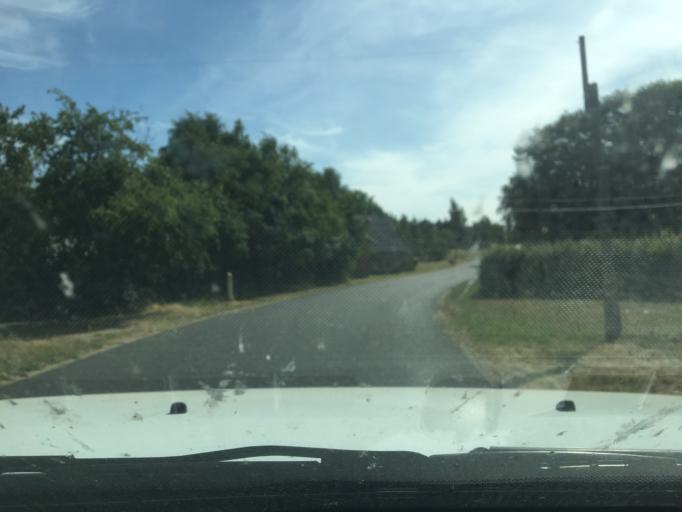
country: DK
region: Central Jutland
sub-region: Viborg Kommune
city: Viborg
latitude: 56.4270
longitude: 9.4529
